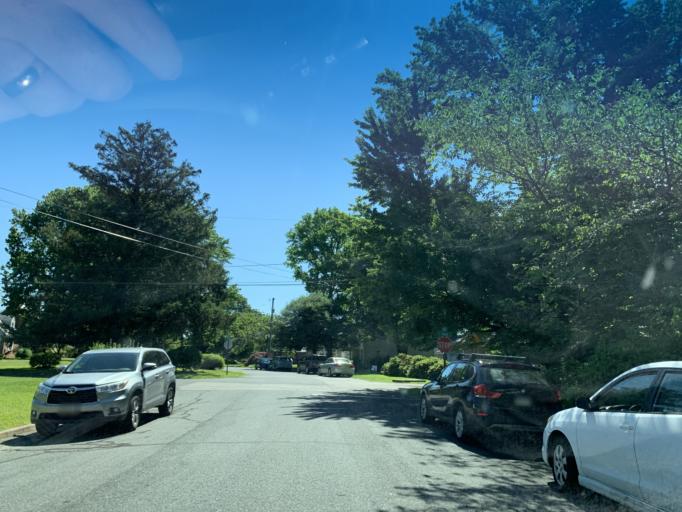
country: US
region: Maryland
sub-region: Harford County
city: Havre de Grace
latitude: 39.5382
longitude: -76.0954
